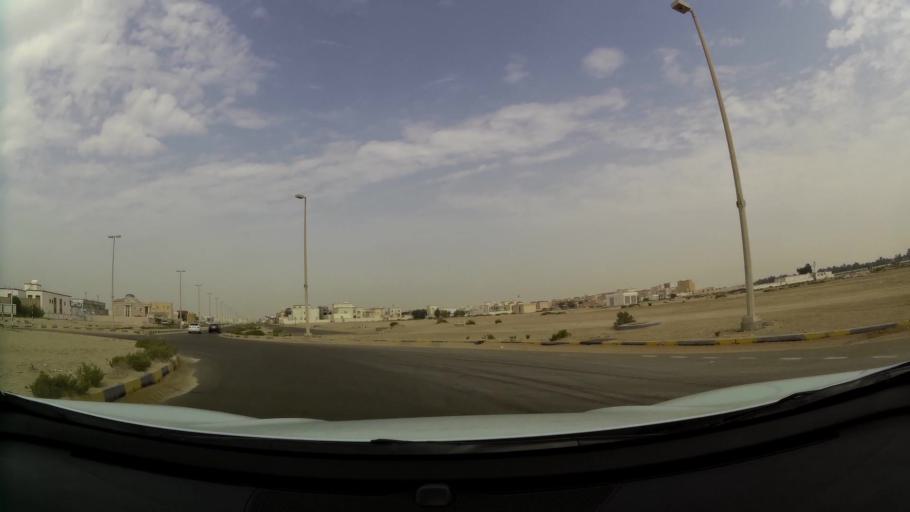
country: AE
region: Abu Dhabi
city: Abu Dhabi
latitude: 24.3035
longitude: 54.6592
